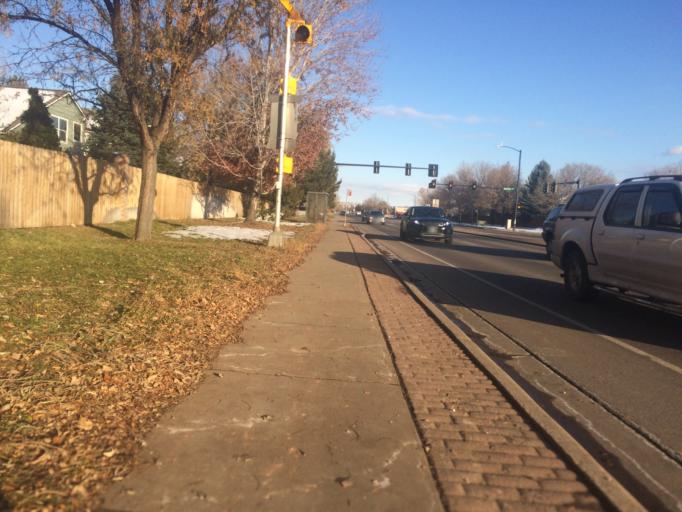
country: US
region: Colorado
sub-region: Boulder County
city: Lafayette
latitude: 39.9870
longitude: -105.1023
